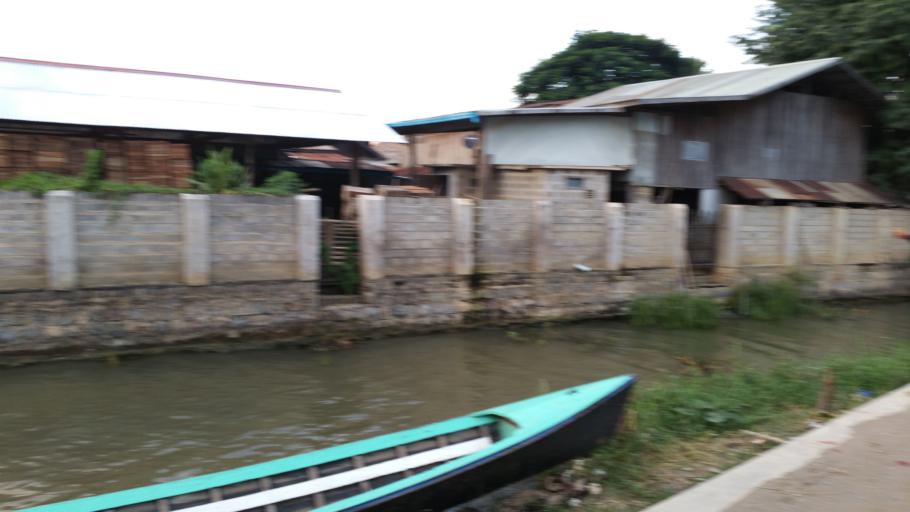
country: MM
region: Shan
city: Taunggyi
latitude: 20.6551
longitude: 96.9248
